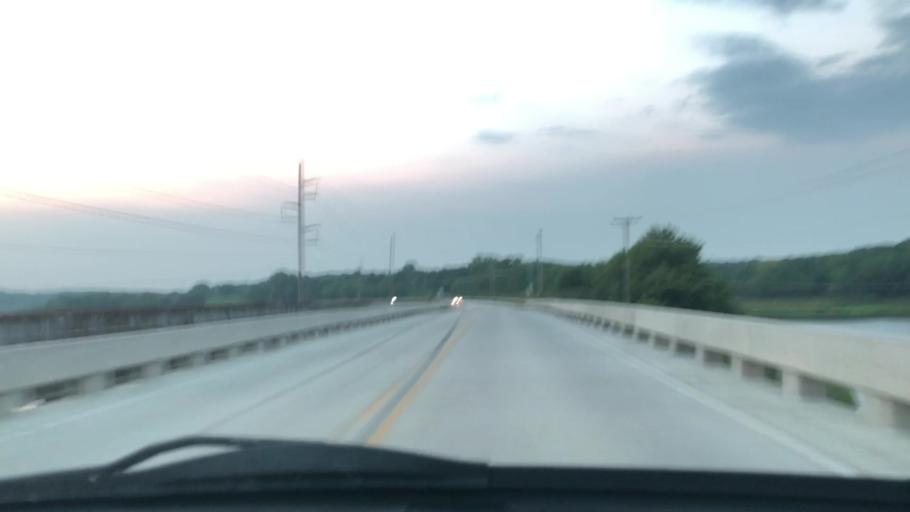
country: US
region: Iowa
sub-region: Johnson County
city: North Liberty
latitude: 41.8065
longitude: -91.6517
